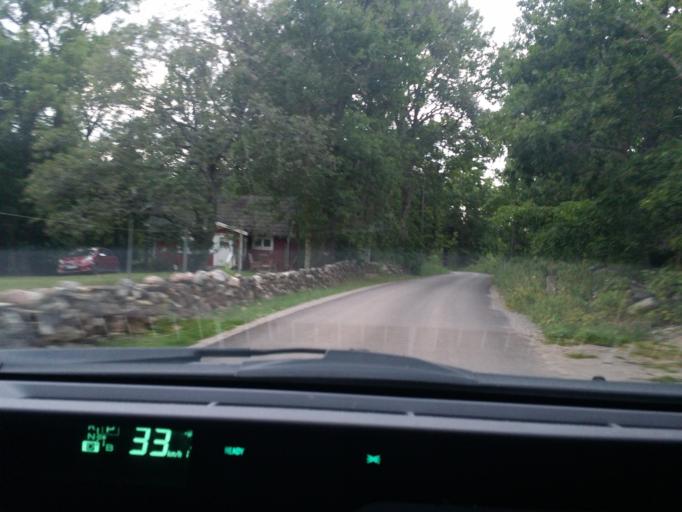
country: SE
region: Kalmar
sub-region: Borgholms Kommun
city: Borgholm
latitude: 57.2060
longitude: 16.9620
